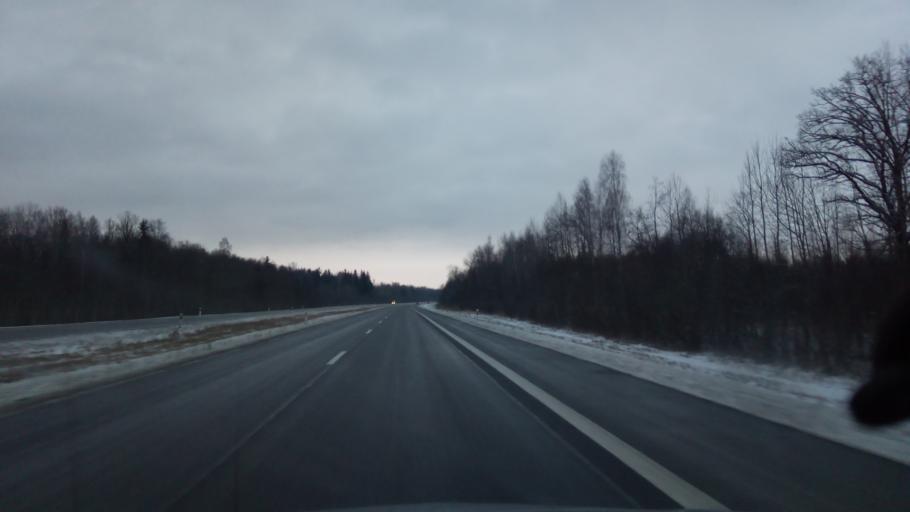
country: LT
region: Vilnius County
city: Ukmerge
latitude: 55.4193
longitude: 24.6879
